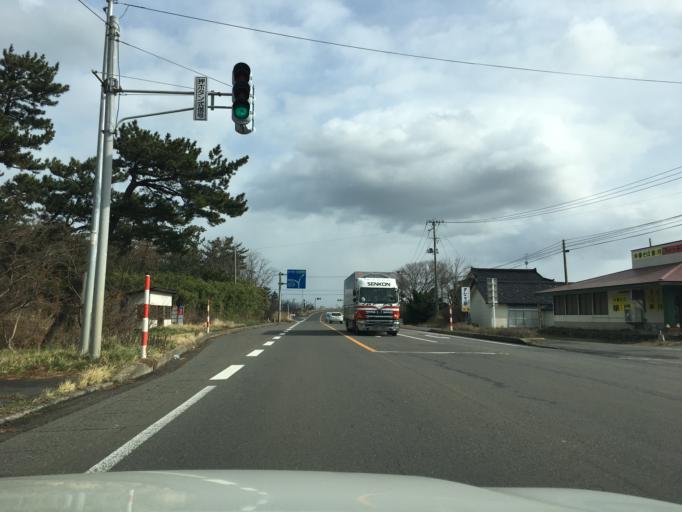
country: JP
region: Yamagata
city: Yuza
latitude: 39.2393
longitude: 139.9123
